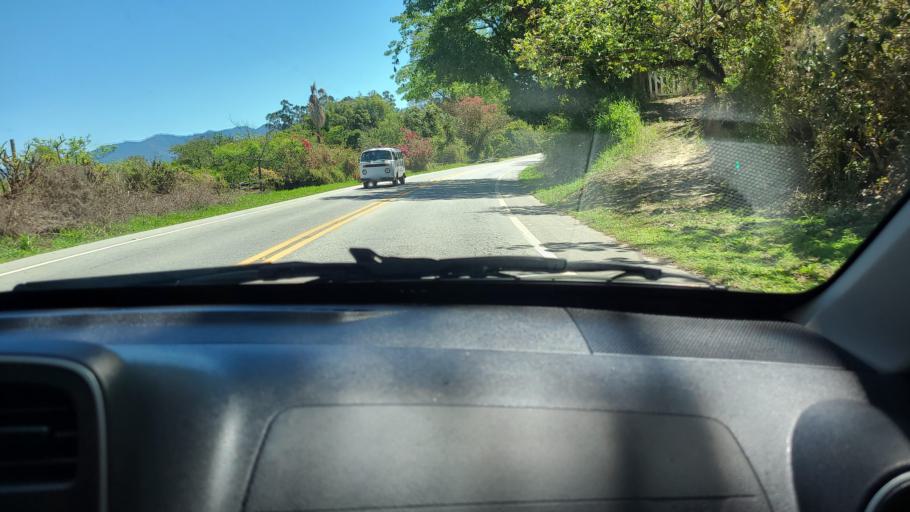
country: BR
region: Sao Paulo
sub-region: Pindamonhangaba
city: Pindamonhangaba
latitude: -22.8966
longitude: -45.5022
